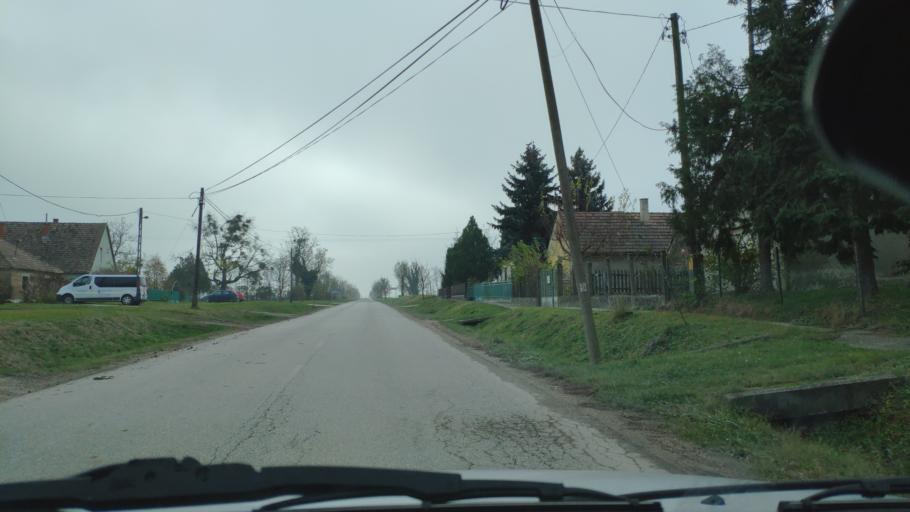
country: HU
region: Somogy
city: Balatonbereny
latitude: 46.6693
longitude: 17.2915
